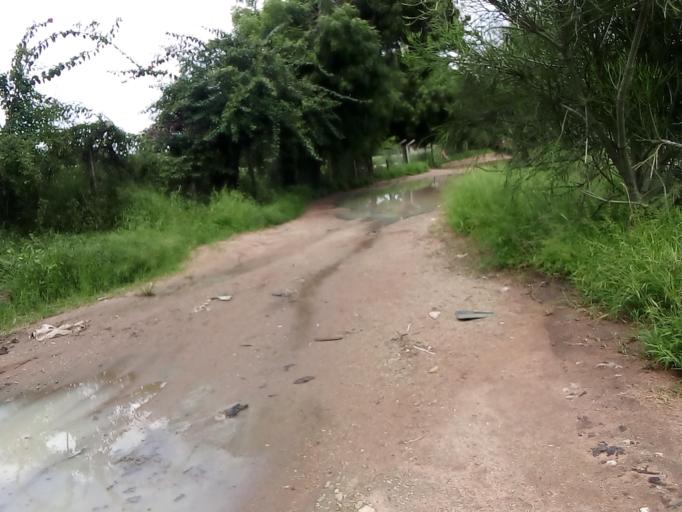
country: TZ
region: Dodoma
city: Dodoma
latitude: -6.1209
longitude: 35.7434
